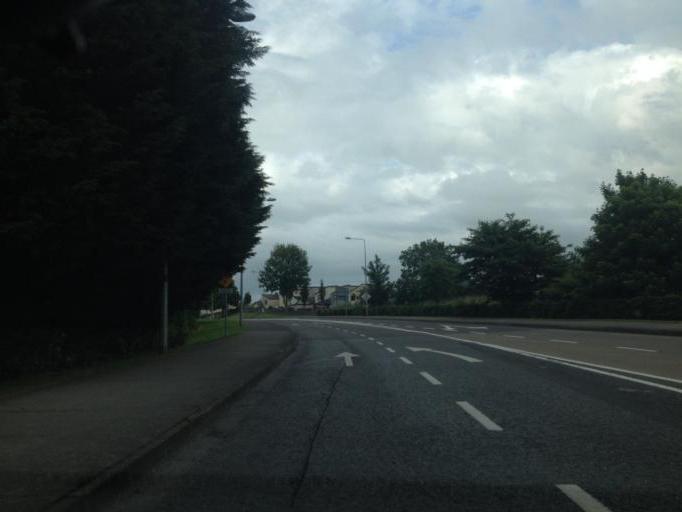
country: IE
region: Connaught
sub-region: Sligo
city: Sligo
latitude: 54.2789
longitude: -8.4737
